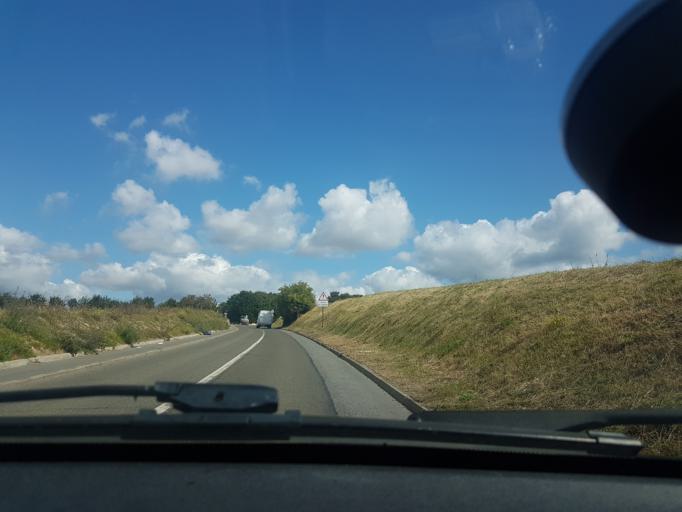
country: FR
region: Ile-de-France
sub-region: Departement des Yvelines
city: Plaisir
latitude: 48.8364
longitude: 1.9436
